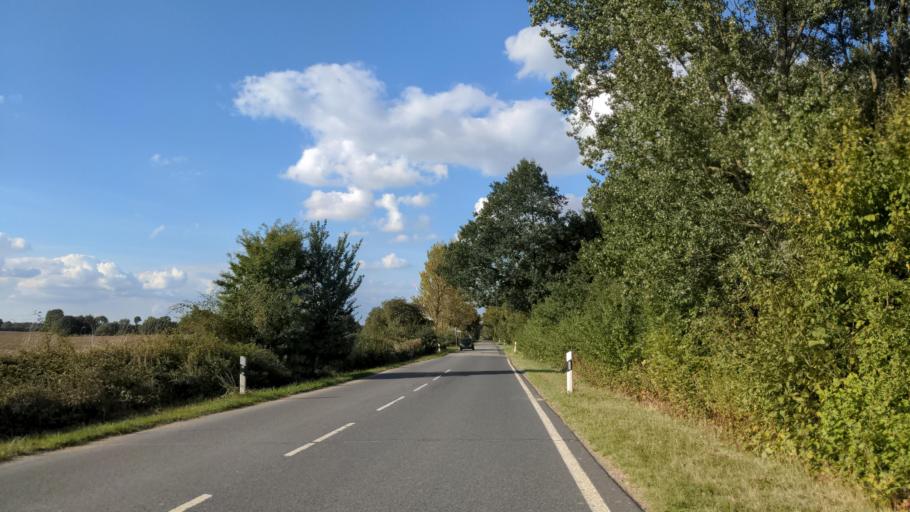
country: DE
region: Schleswig-Holstein
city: Monkhagen
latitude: 53.9128
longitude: 10.5534
